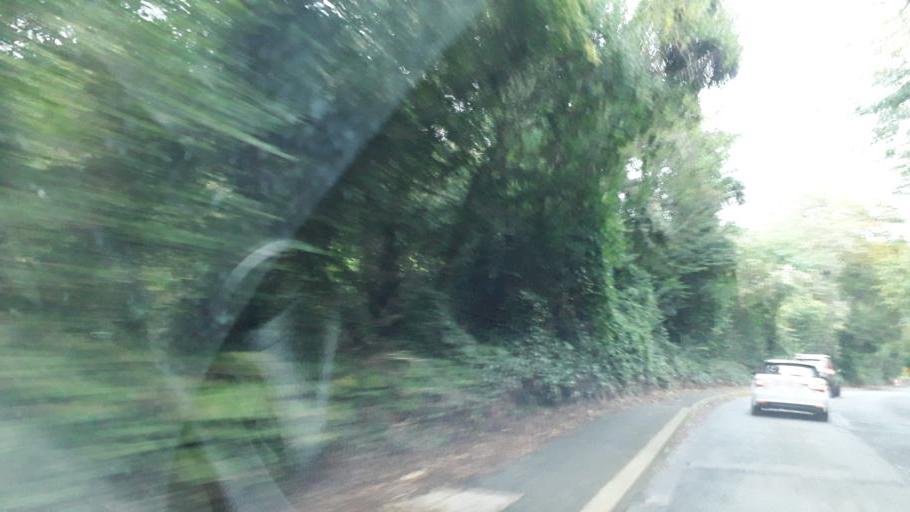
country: IE
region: Leinster
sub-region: Wicklow
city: Enniskerry
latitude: 53.1895
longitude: -6.1510
